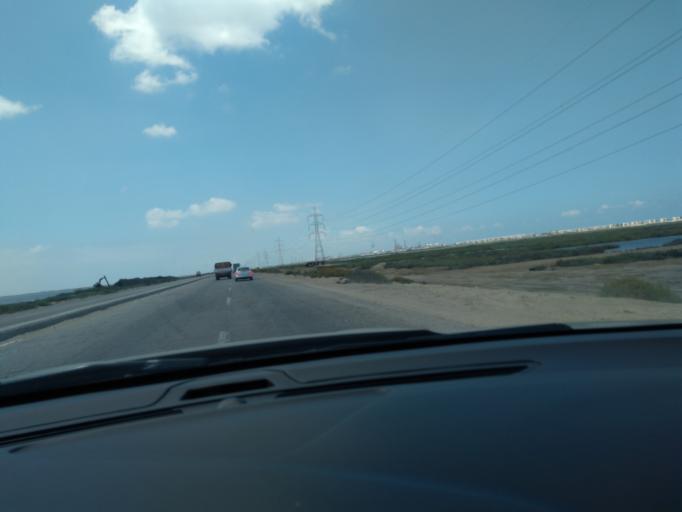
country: EG
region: Muhafazat Bur Sa`id
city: Port Said
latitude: 31.2803
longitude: 32.1911
